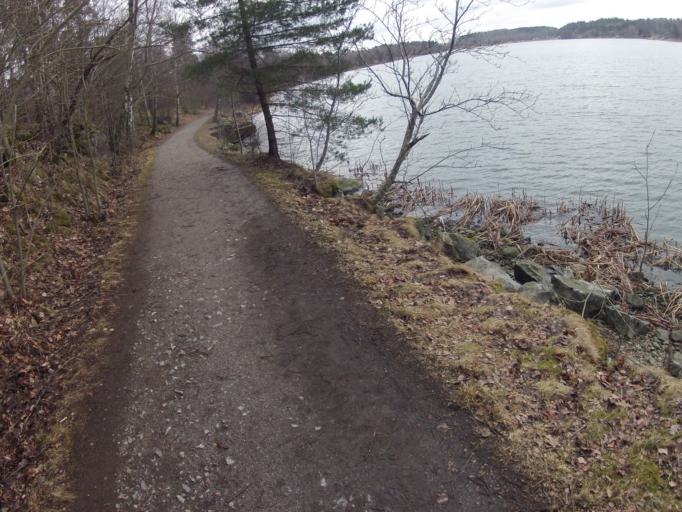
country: SE
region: Stockholm
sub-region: Norrtalje Kommun
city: Bergshamra
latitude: 59.3705
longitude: 18.0316
